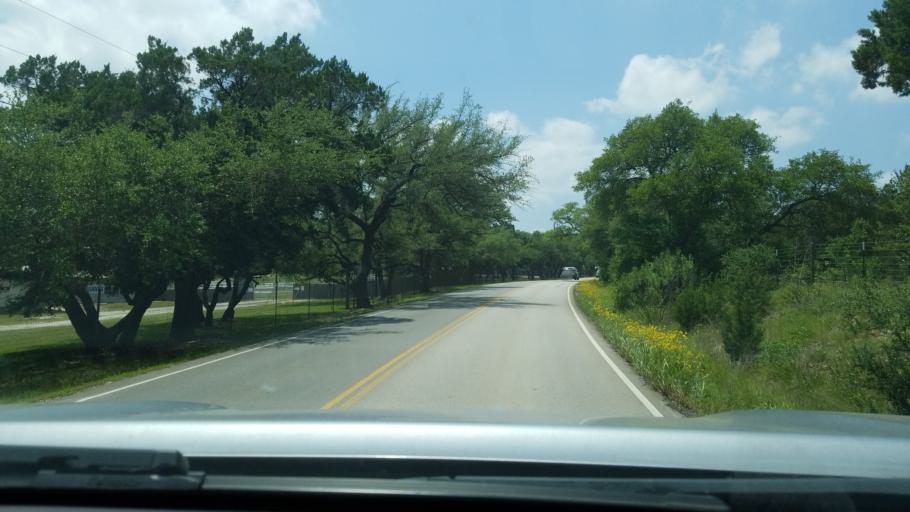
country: US
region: Texas
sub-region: Hays County
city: Woodcreek
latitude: 30.0434
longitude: -98.1068
